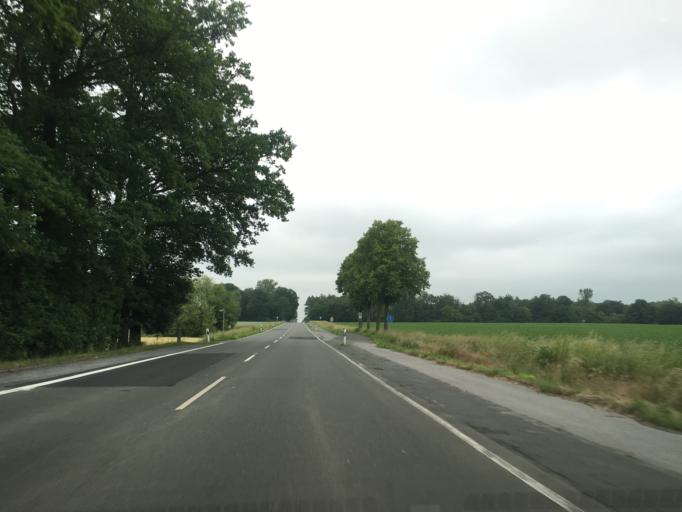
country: DE
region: North Rhine-Westphalia
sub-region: Regierungsbezirk Munster
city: Steinfurt
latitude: 52.1224
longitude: 7.3374
